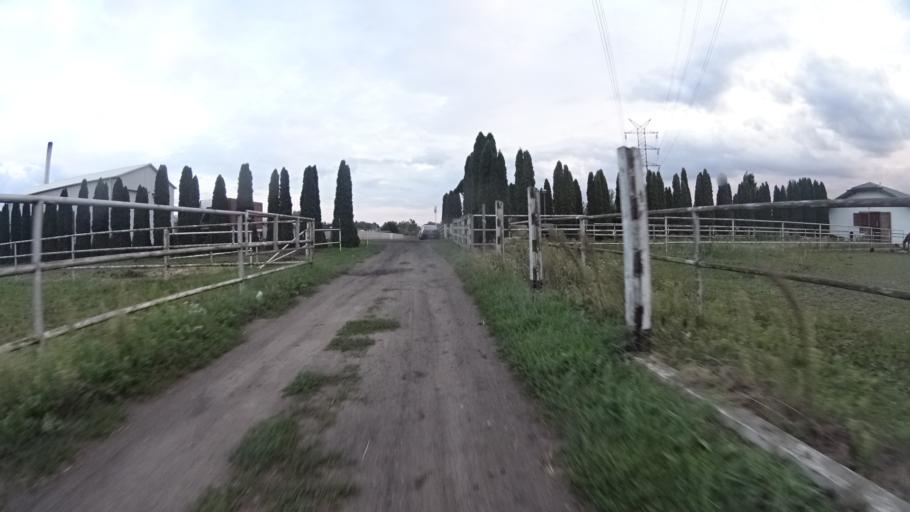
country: PL
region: Masovian Voivodeship
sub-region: Powiat warszawski zachodni
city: Ozarow Mazowiecki
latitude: 52.2366
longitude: 20.7657
